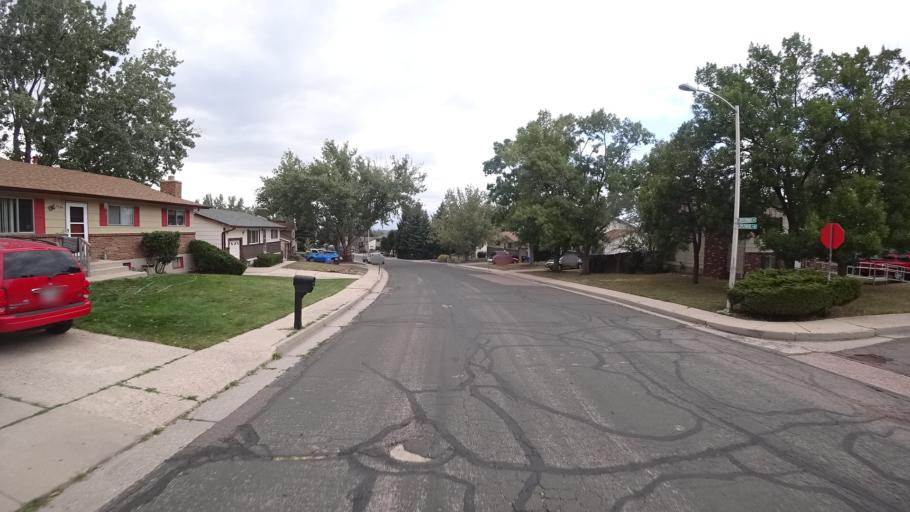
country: US
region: Colorado
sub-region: El Paso County
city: Cimarron Hills
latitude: 38.8934
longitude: -104.7367
